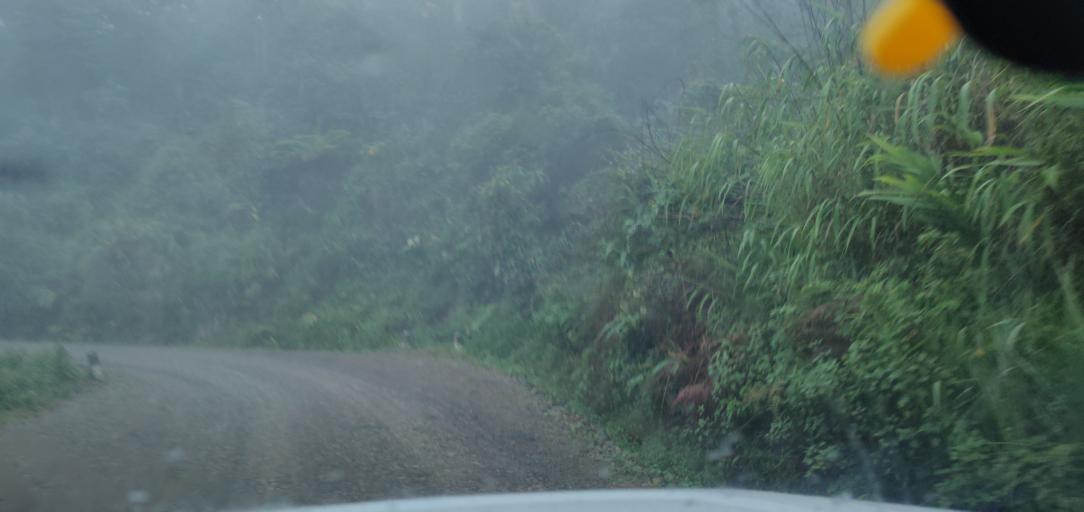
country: LA
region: Phongsali
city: Phongsali
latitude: 21.3968
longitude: 102.1922
